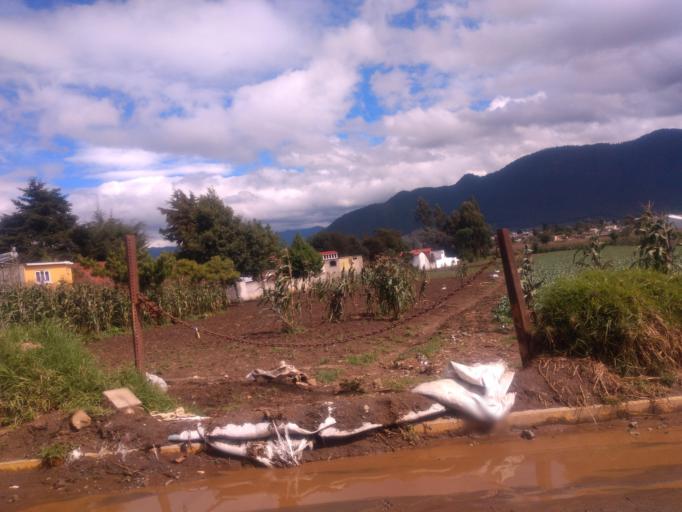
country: GT
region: Quetzaltenango
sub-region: Municipio de La Esperanza
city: La Esperanza
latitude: 14.8609
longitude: -91.5723
